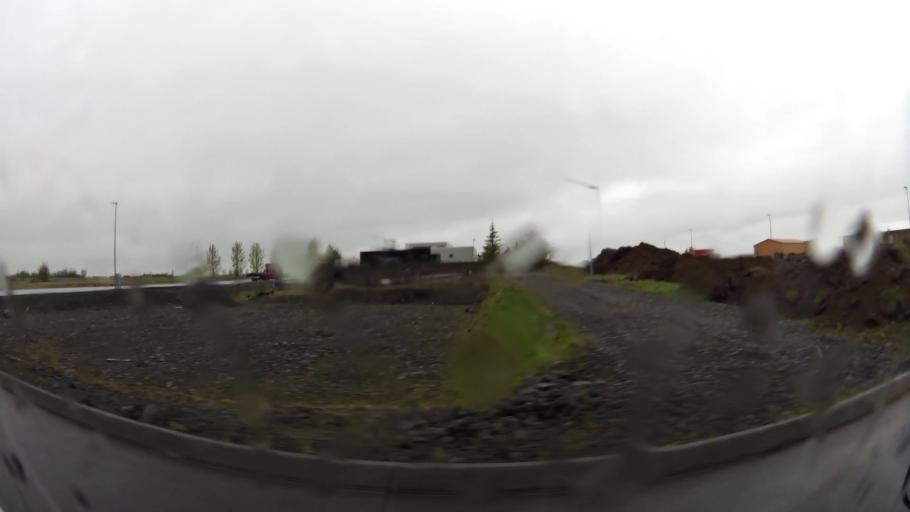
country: IS
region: South
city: Selfoss
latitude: 63.9287
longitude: -21.0298
